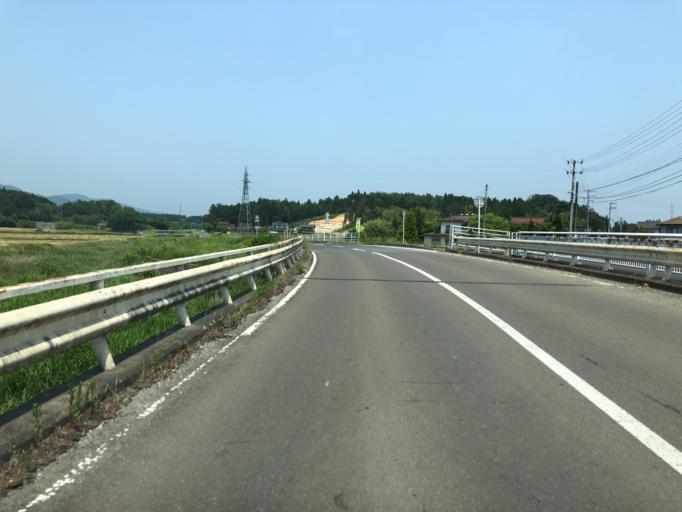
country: JP
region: Miyagi
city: Marumori
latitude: 37.8317
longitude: 140.8958
